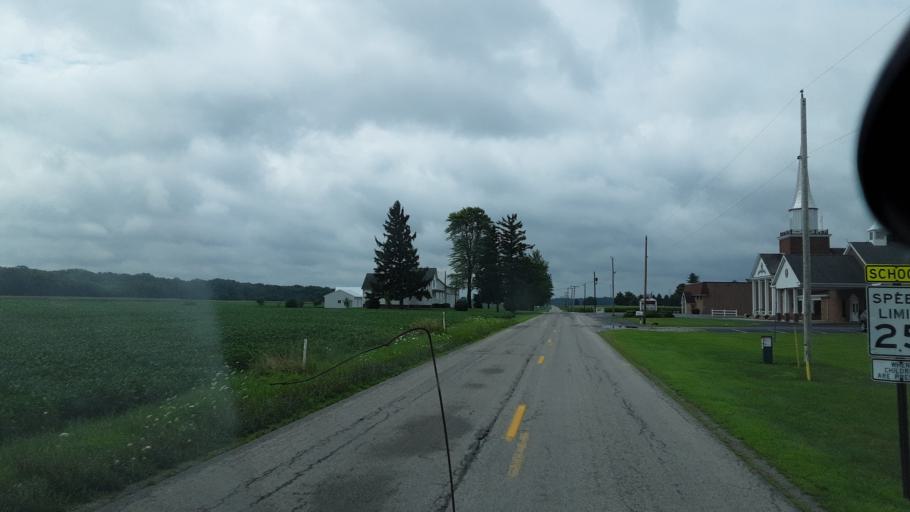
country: US
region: Indiana
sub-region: Allen County
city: Monroeville
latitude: 40.9693
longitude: -84.9691
